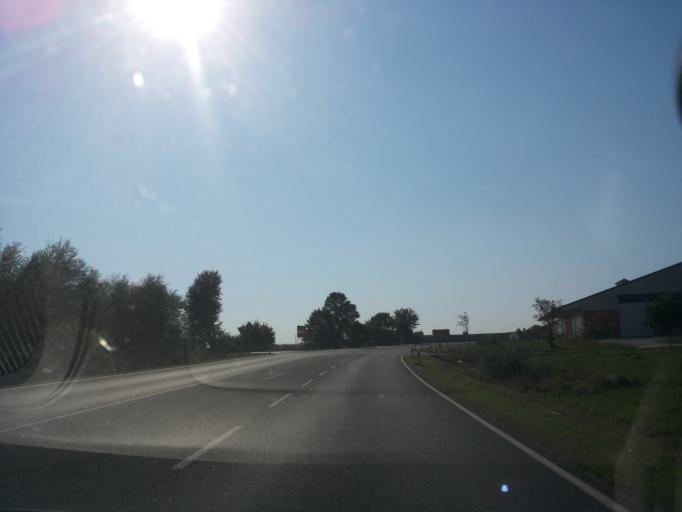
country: DE
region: Bavaria
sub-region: Lower Bavaria
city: Neustadt an der Donau
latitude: 48.8168
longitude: 11.7126
